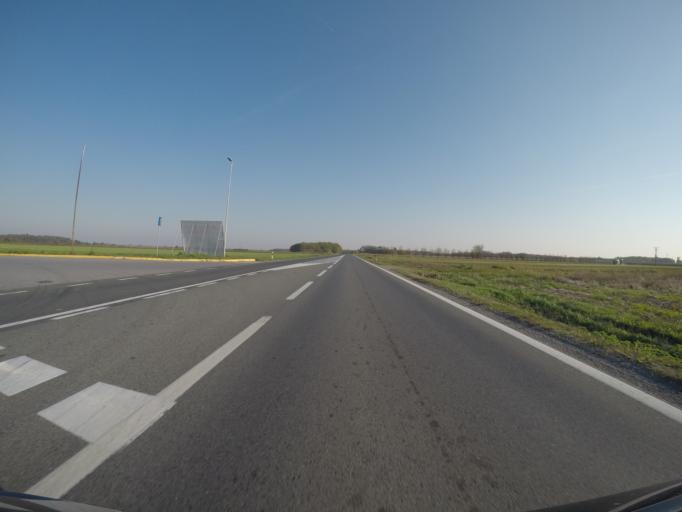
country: HR
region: Virovitick-Podravska
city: Pitomaca
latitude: 45.9756
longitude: 17.1708
